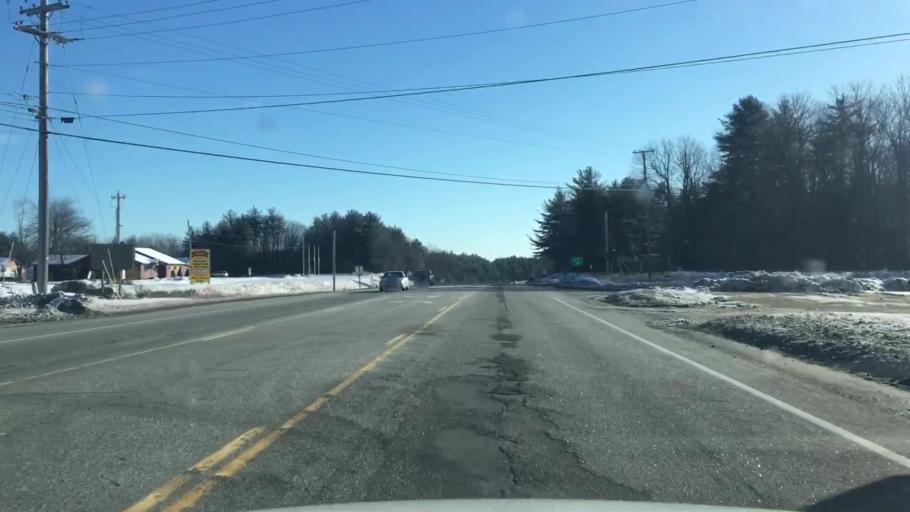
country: US
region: Maine
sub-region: Androscoggin County
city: Turner
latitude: 44.1859
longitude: -70.2360
